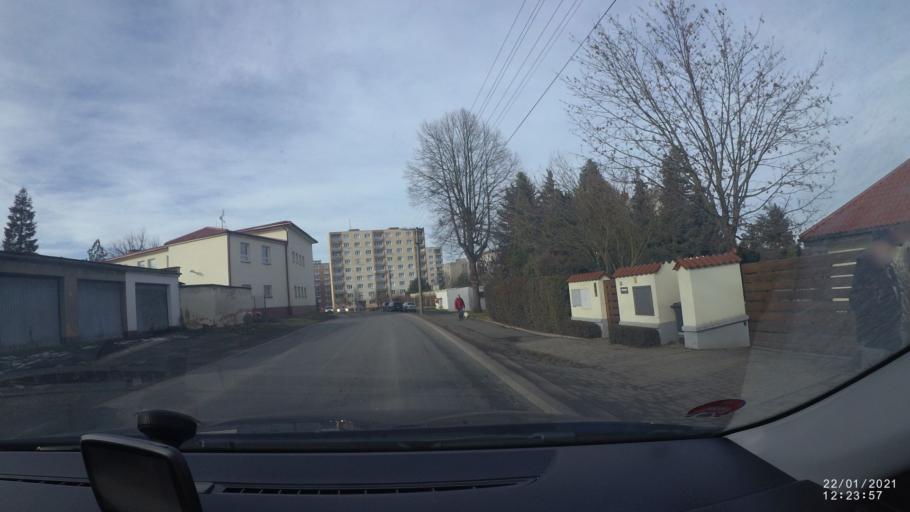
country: CZ
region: Plzensky
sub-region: Okres Plzen-Mesto
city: Pilsen
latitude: 49.7577
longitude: 13.4254
